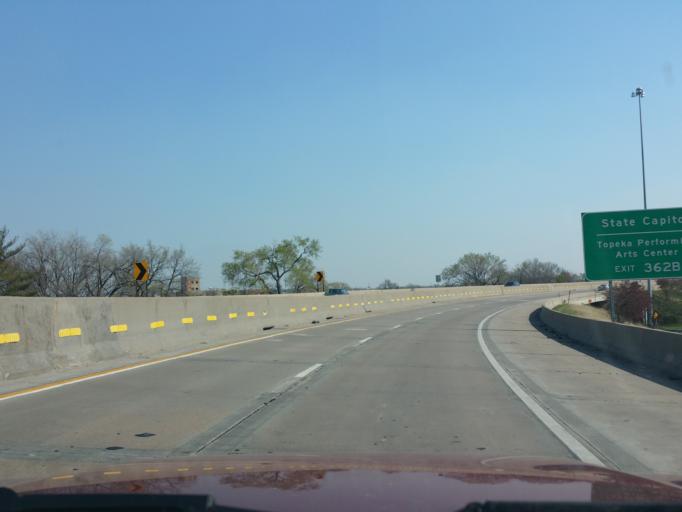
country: US
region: Kansas
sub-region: Shawnee County
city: Topeka
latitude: 39.0562
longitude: -95.6686
